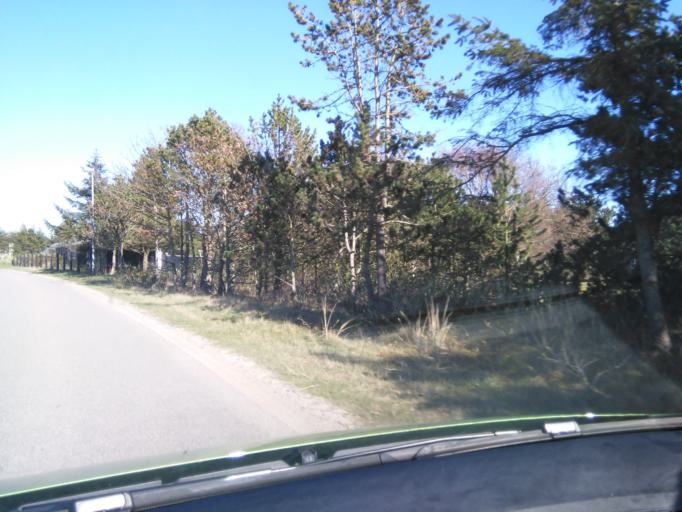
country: DK
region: South Denmark
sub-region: Varde Kommune
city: Oksbol
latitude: 55.5527
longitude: 8.1202
